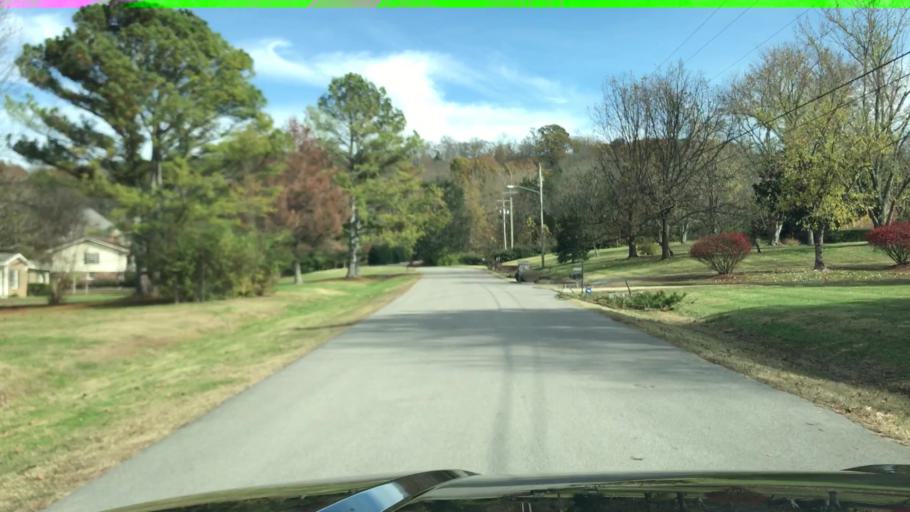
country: US
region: Tennessee
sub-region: Davidson County
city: Forest Hills
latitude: 36.0248
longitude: -86.8472
